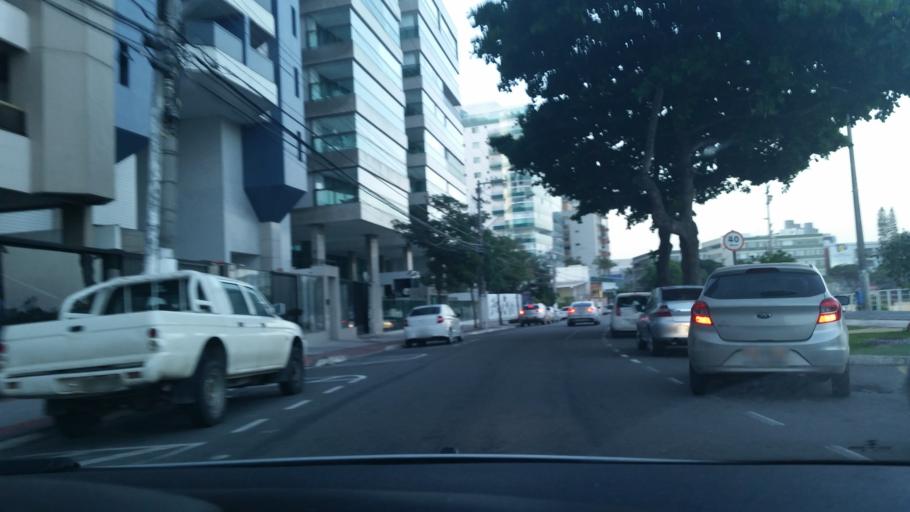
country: BR
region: Espirito Santo
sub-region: Vila Velha
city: Vila Velha
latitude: -20.3308
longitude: -40.2740
